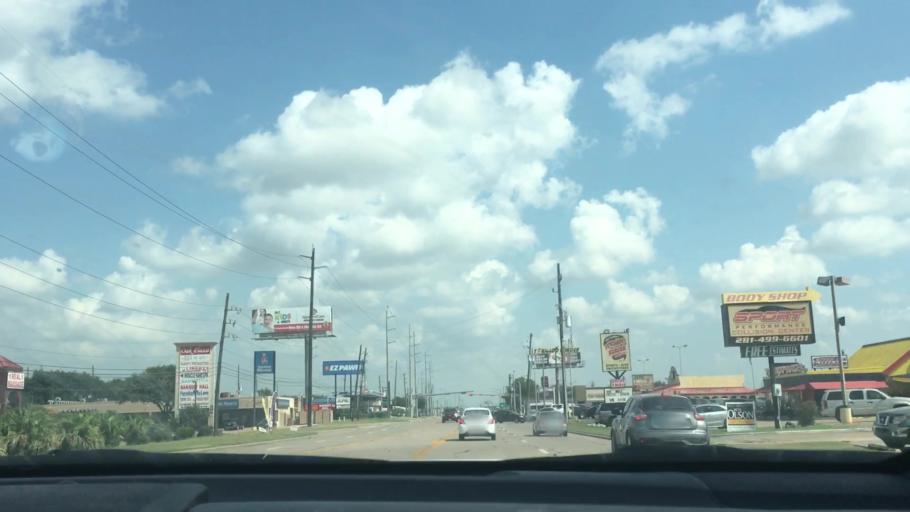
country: US
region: Texas
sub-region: Fort Bend County
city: Stafford
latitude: 29.6109
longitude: -95.5645
